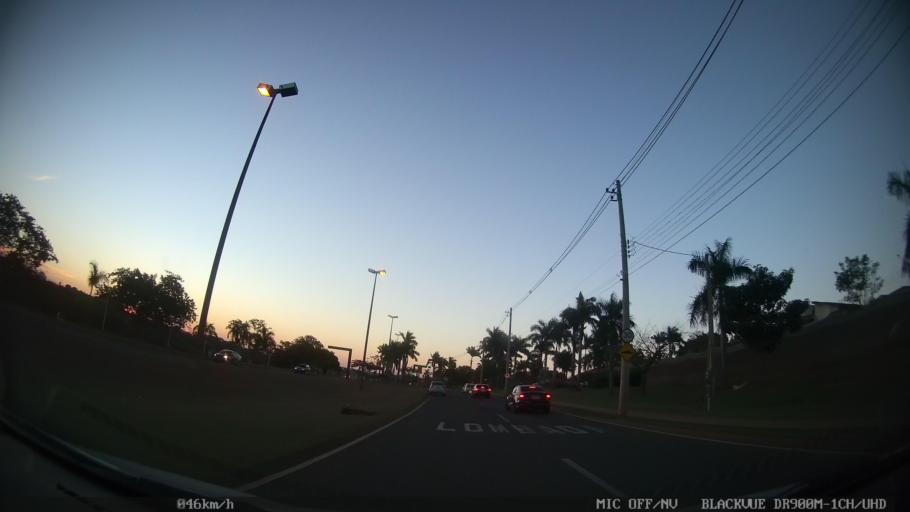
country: BR
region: Sao Paulo
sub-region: Sao Jose Do Rio Preto
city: Sao Jose do Rio Preto
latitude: -20.8211
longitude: -49.3449
